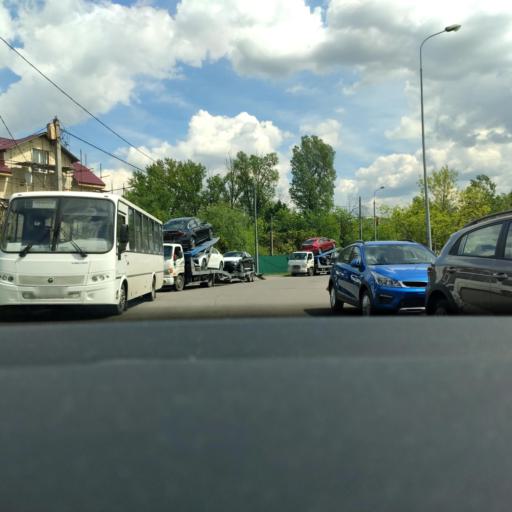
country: RU
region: Moscow
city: Vagonoremont
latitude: 55.9078
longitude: 37.5525
